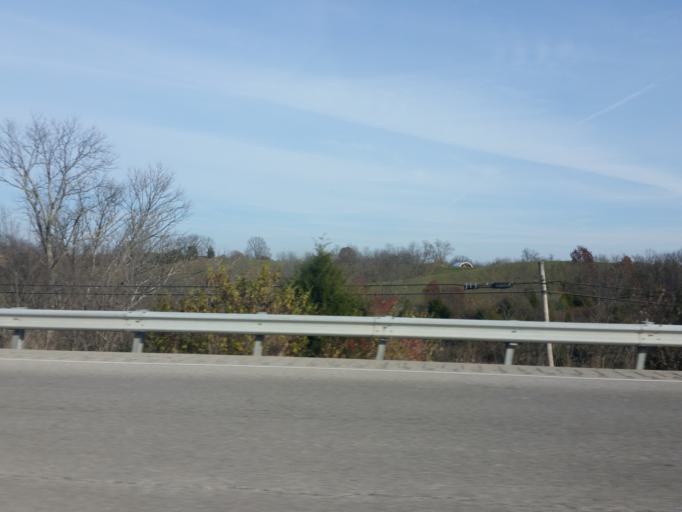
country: US
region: Kentucky
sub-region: Harrison County
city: Cynthiana
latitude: 38.4710
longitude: -84.2848
